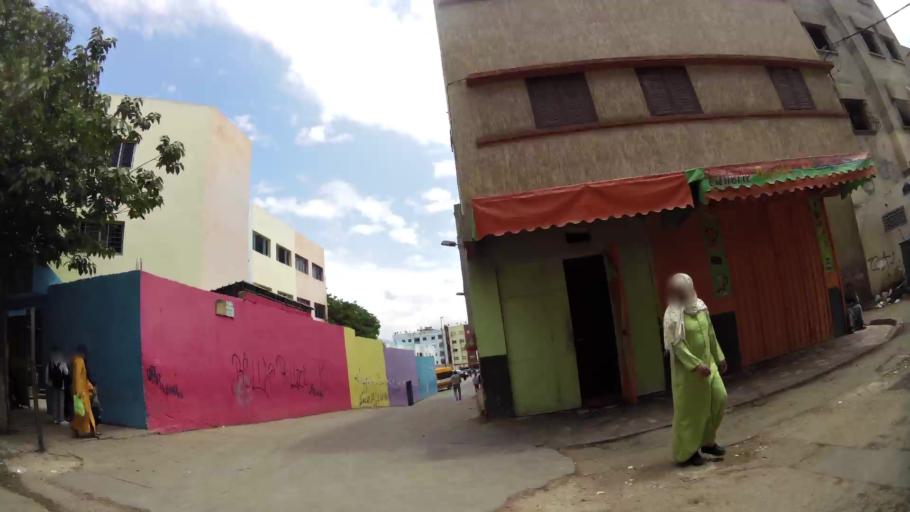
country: MA
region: Rabat-Sale-Zemmour-Zaer
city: Sale
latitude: 34.0514
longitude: -6.8175
